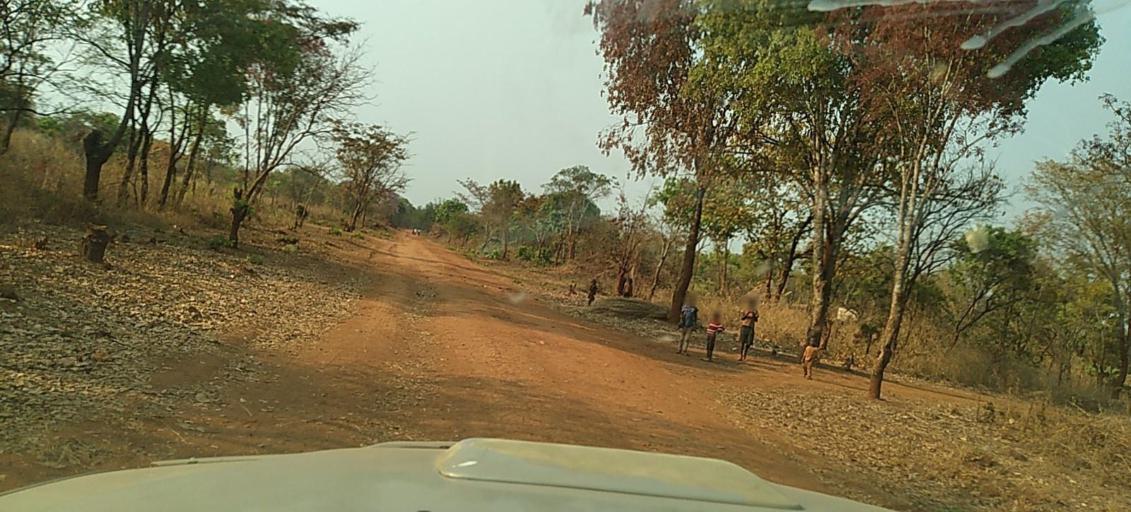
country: ZM
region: North-Western
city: Kasempa
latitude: -13.2978
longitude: 26.5543
